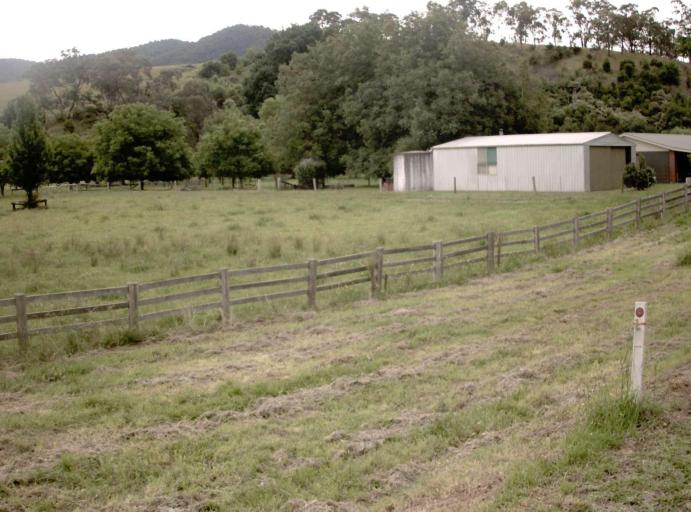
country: AU
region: Victoria
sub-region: East Gippsland
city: Bairnsdale
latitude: -37.4637
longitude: 147.2503
